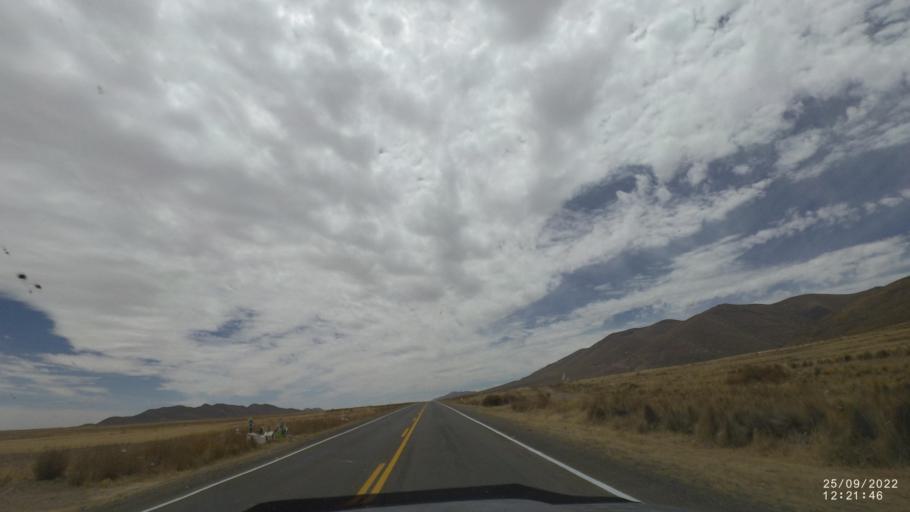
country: BO
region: Oruro
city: Poopo
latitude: -18.4054
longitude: -66.9768
